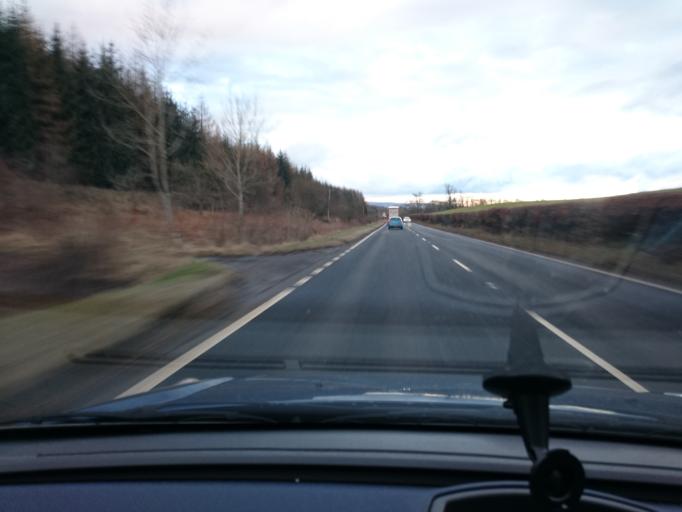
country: GB
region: Scotland
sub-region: Stirling
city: Doune
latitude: 56.2034
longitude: -4.0968
